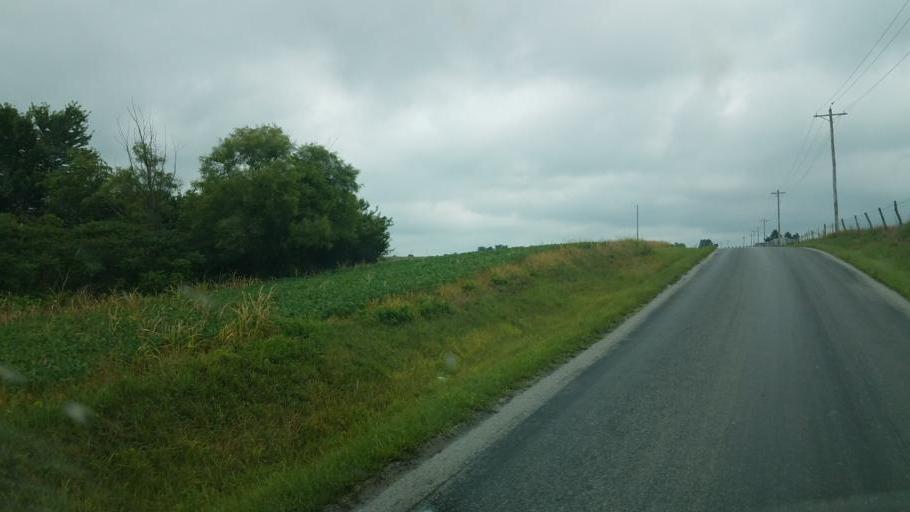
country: US
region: Ohio
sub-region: Highland County
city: Leesburg
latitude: 39.2375
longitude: -83.4748
